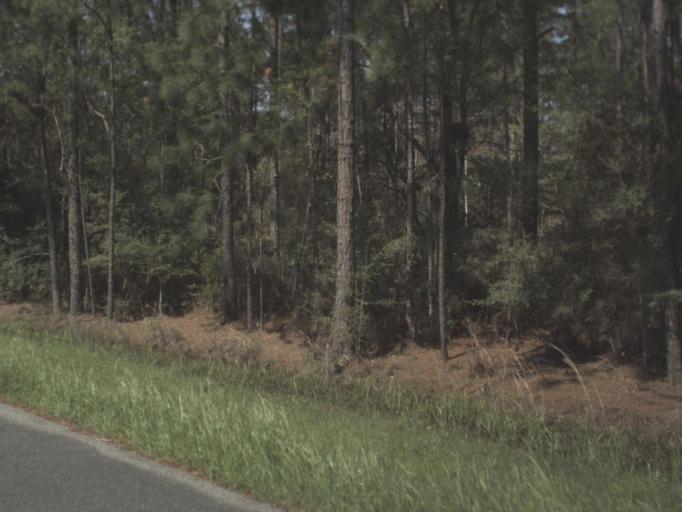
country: US
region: Florida
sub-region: Holmes County
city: Bonifay
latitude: 30.7513
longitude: -85.8893
